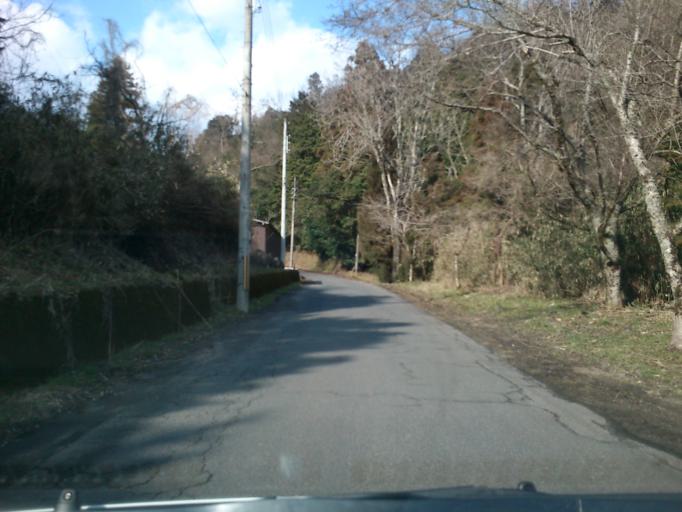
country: JP
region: Kyoto
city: Miyazu
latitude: 35.5825
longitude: 135.1773
